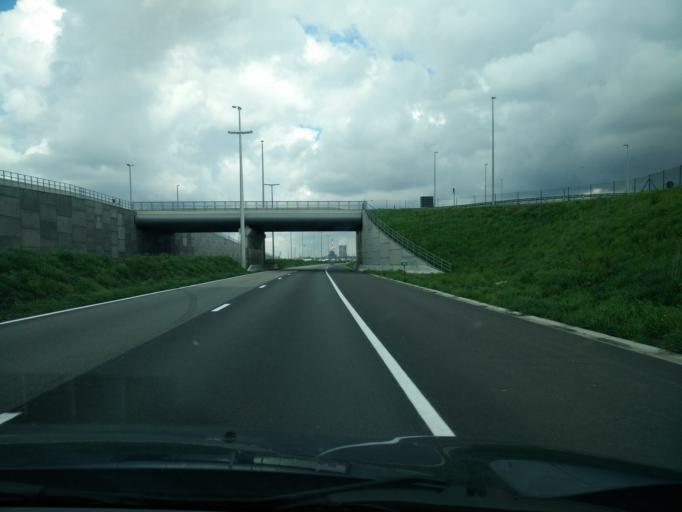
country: BE
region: Flanders
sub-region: Provincie Oost-Vlaanderen
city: Evergem
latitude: 51.1038
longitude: 3.7588
